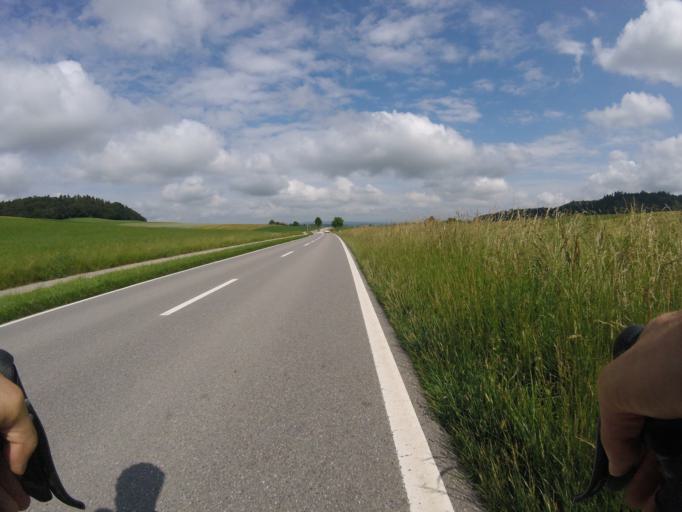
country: CH
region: Bern
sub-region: Emmental District
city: Krauchthal
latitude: 47.0237
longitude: 7.5544
